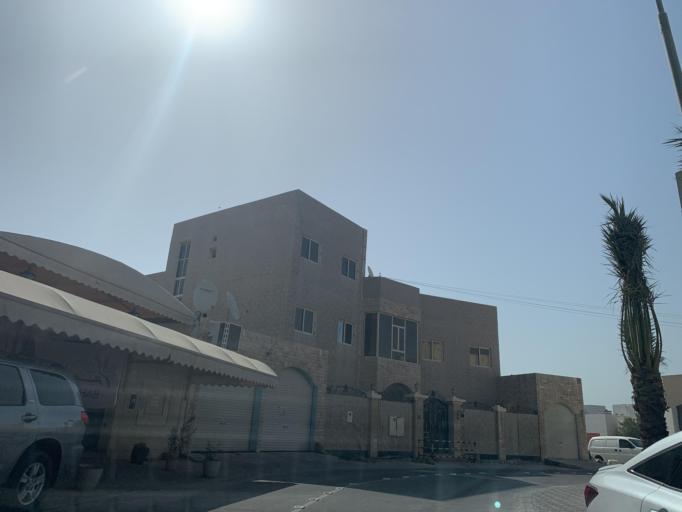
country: BH
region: Muharraq
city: Al Muharraq
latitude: 26.2716
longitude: 50.6019
